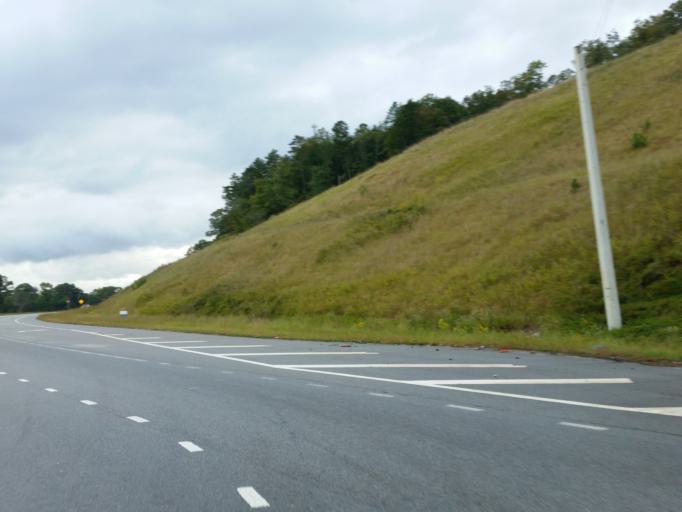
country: US
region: Georgia
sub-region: Bartow County
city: Emerson
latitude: 34.1191
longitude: -84.7683
